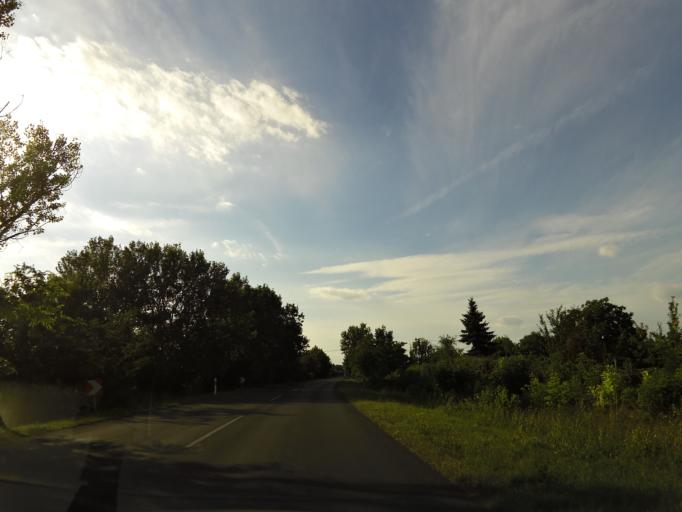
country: HU
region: Csongrad
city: Szatymaz
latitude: 46.3528
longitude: 20.0559
